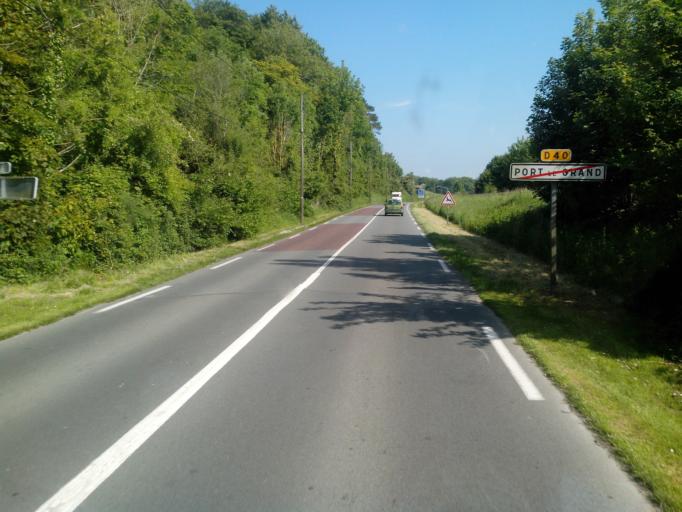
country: FR
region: Picardie
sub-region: Departement de la Somme
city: Sailly-Flibeaucourt
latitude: 50.1486
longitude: 1.7530
